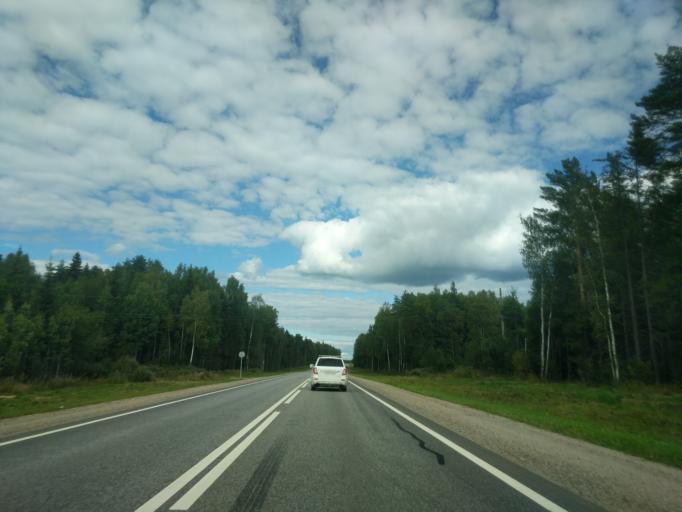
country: RU
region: Kostroma
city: Ostrovskoye
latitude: 57.8099
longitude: 42.4185
